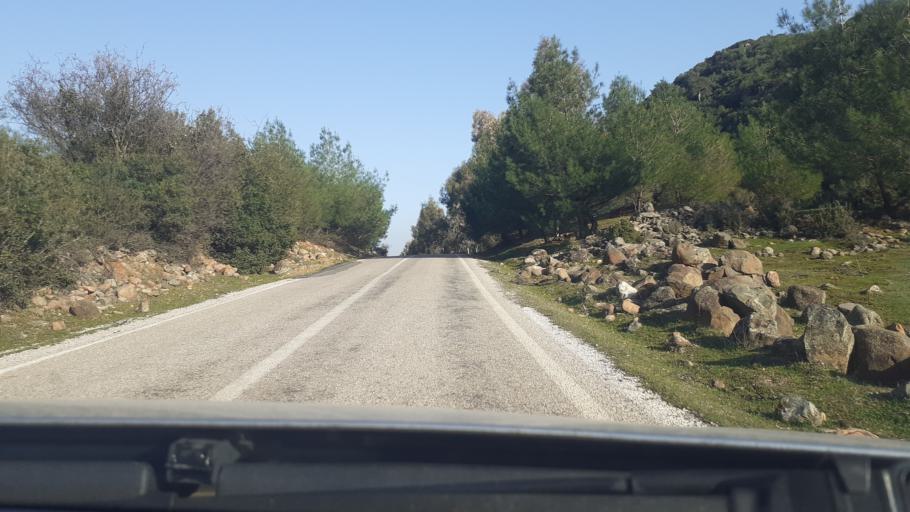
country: TR
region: Hatay
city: Aktepe
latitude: 36.7331
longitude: 36.4722
